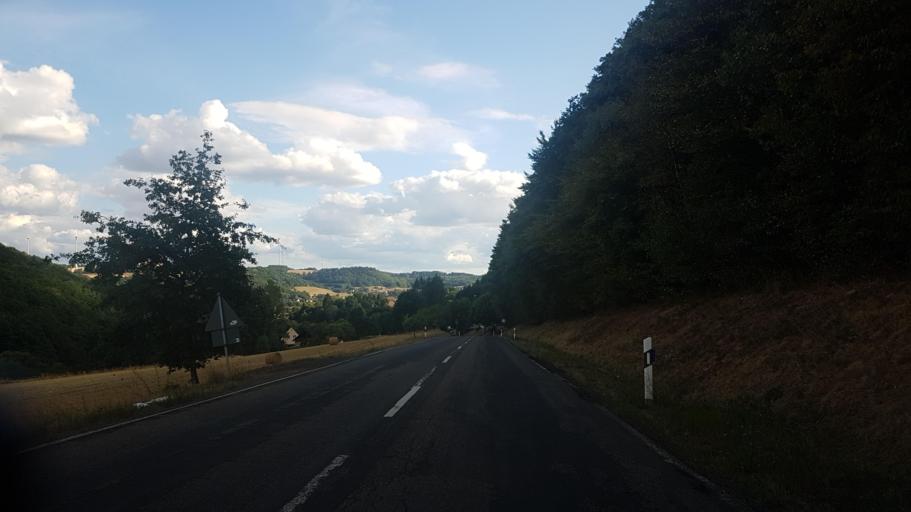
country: DE
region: Rheinland-Pfalz
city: Dienstweiler
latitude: 49.6288
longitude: 7.1932
